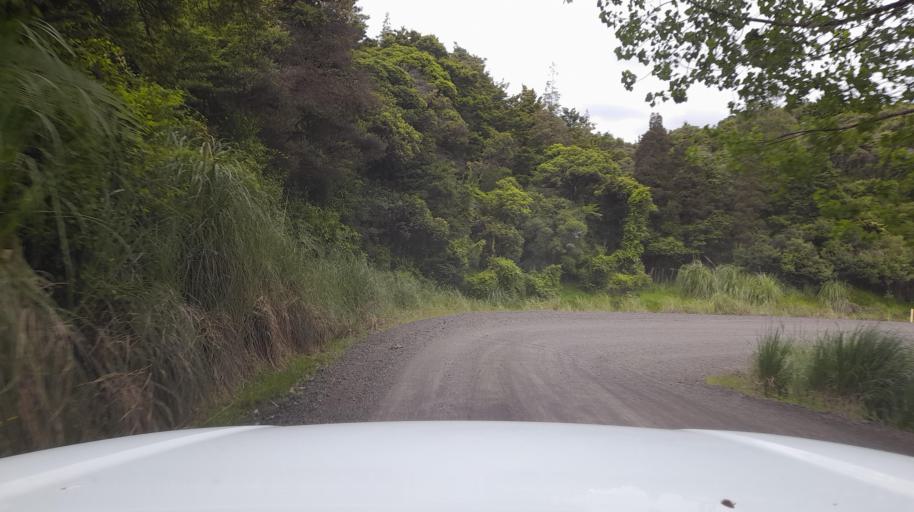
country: NZ
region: Northland
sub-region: Far North District
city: Kaitaia
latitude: -35.3267
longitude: 173.3529
